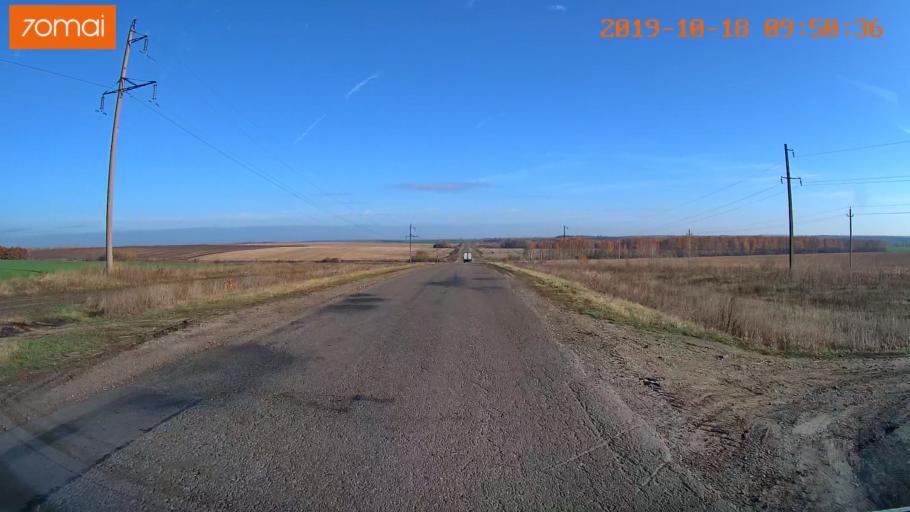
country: RU
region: Tula
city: Kazachka
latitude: 53.3306
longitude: 38.2797
